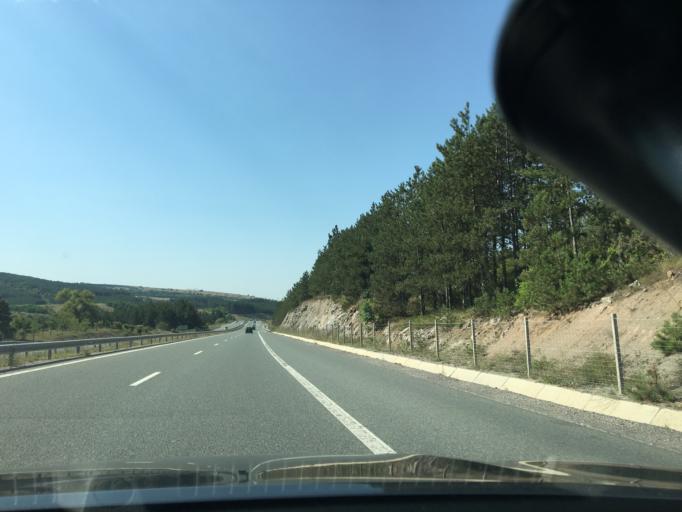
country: BG
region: Pernik
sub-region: Obshtina Pernik
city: Pernik
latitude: 42.5052
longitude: 23.1408
